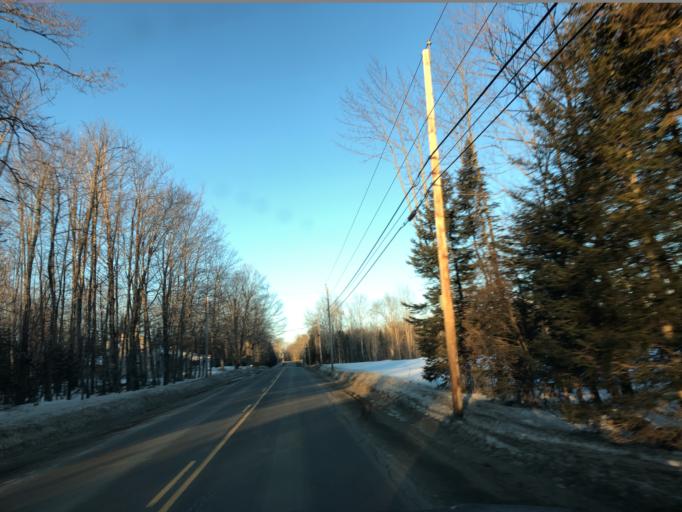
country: US
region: Maine
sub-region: Penobscot County
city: Charleston
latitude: 45.0097
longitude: -69.0052
